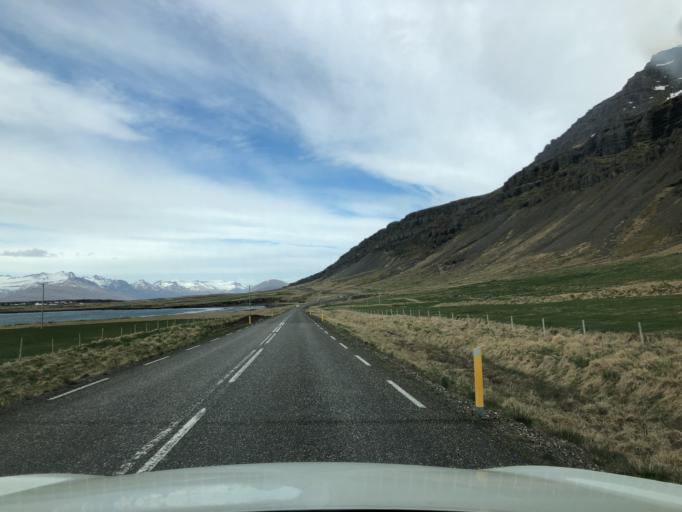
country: IS
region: East
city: Eskifjoerdur
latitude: 64.7952
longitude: -13.9537
